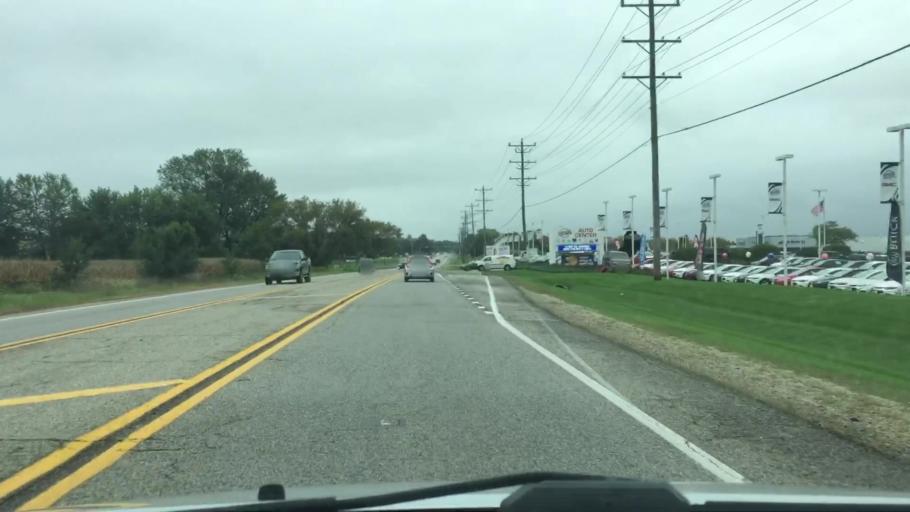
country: US
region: Illinois
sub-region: McHenry County
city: McHenry
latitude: 42.3135
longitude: -88.2777
